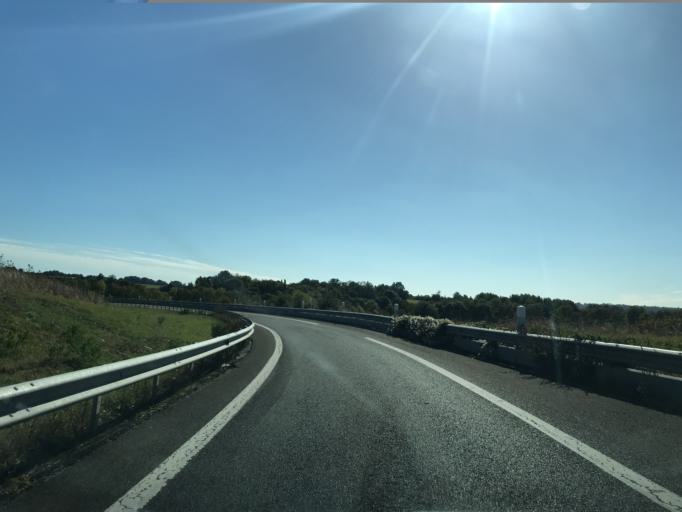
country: FR
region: Ile-de-France
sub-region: Departement de Seine-et-Marne
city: Bouleurs
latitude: 48.8854
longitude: 2.8907
